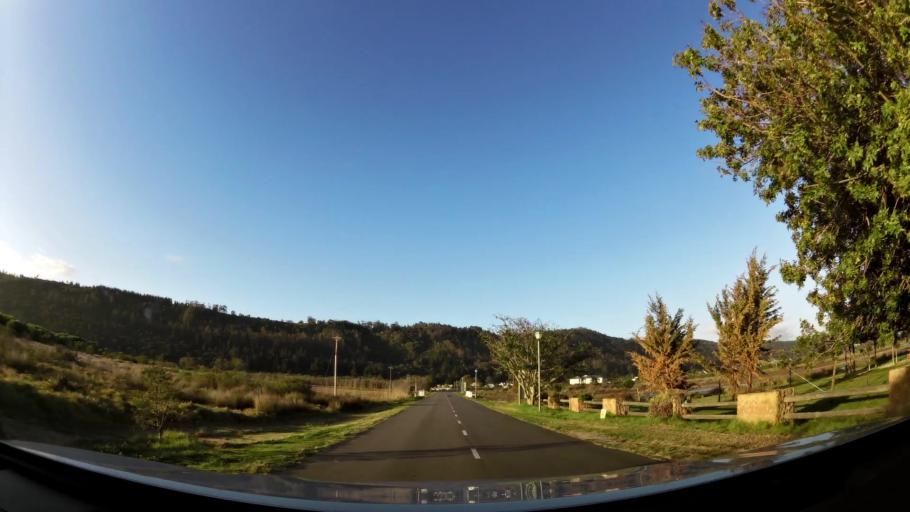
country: ZA
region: Western Cape
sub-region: Eden District Municipality
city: Knysna
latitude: -34.0143
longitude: 22.7880
